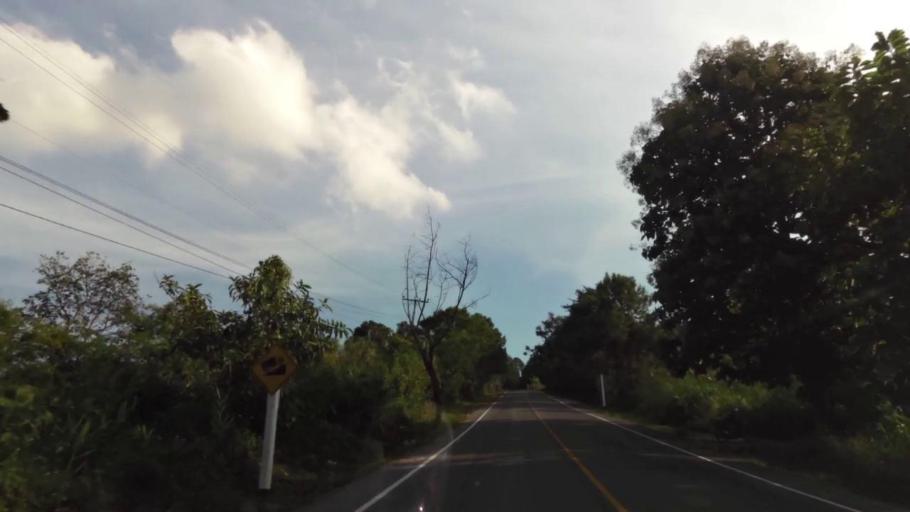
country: TH
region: Chiang Rai
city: Khun Tan
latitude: 19.8737
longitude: 100.3207
